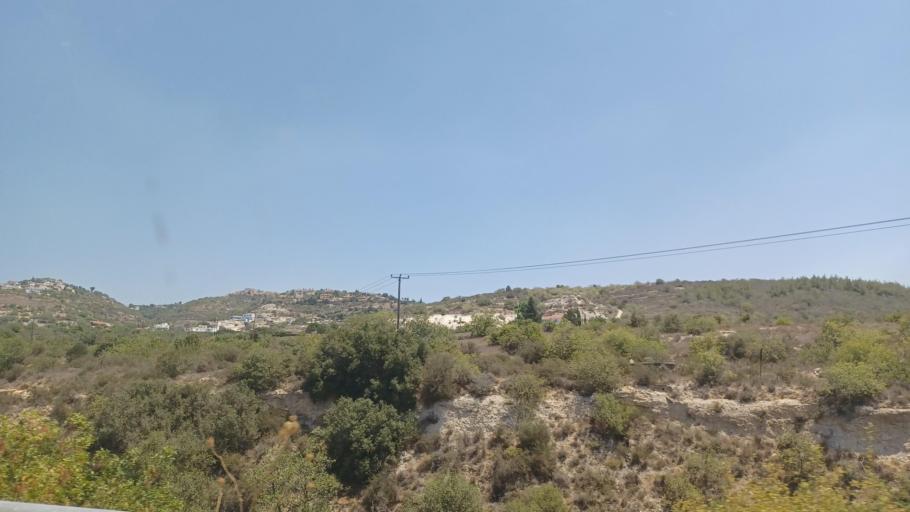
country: CY
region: Pafos
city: Mesogi
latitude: 34.8223
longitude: 32.4589
